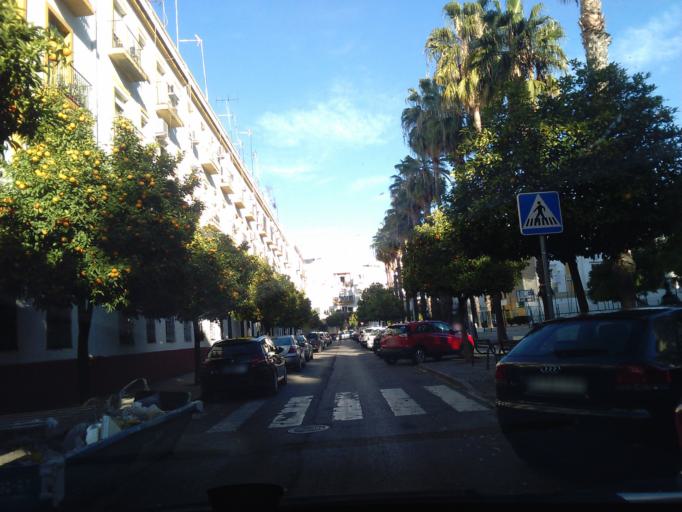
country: ES
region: Andalusia
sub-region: Provincia de Sevilla
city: Sevilla
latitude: 37.3540
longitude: -5.9774
